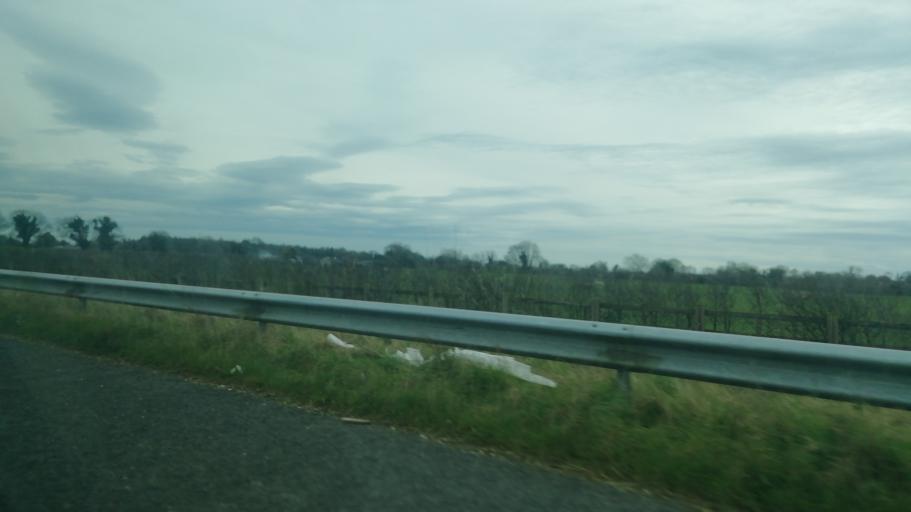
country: IE
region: Leinster
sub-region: Uibh Fhaili
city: Edenderry
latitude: 53.3450
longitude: -7.0045
